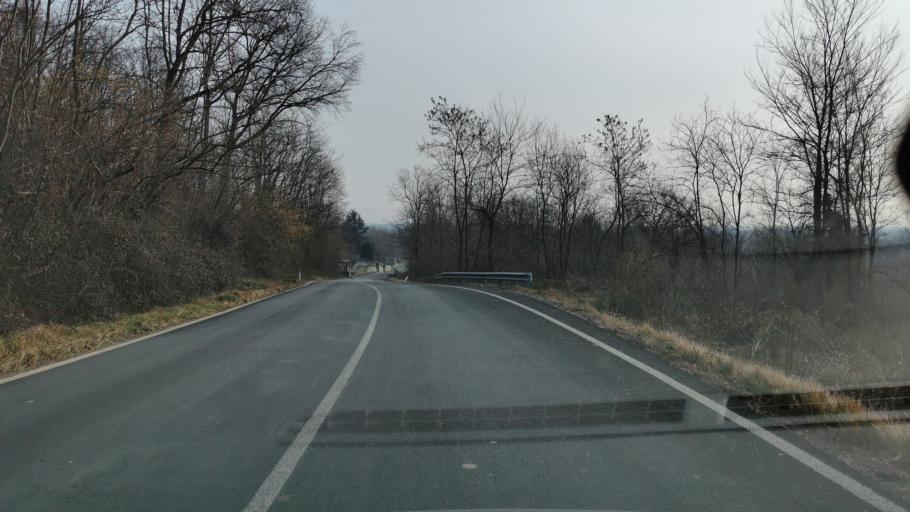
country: IT
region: Piedmont
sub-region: Provincia di Torino
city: Barbania
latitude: 45.2907
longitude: 7.6494
